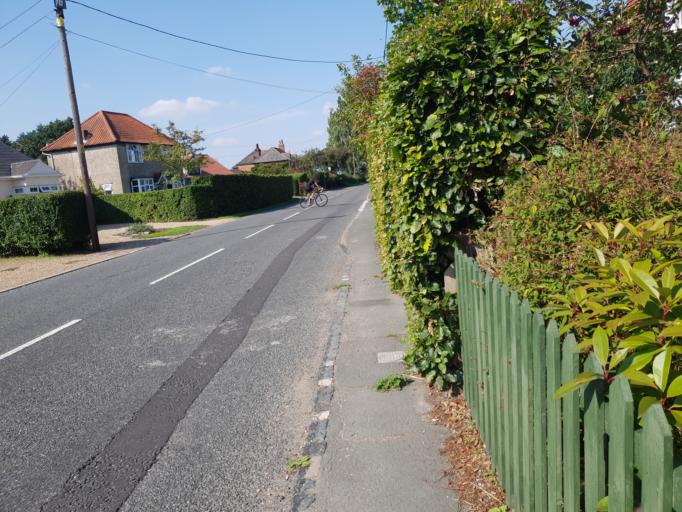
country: GB
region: England
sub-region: Suffolk
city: East Bergholt
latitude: 51.9457
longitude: 0.9958
